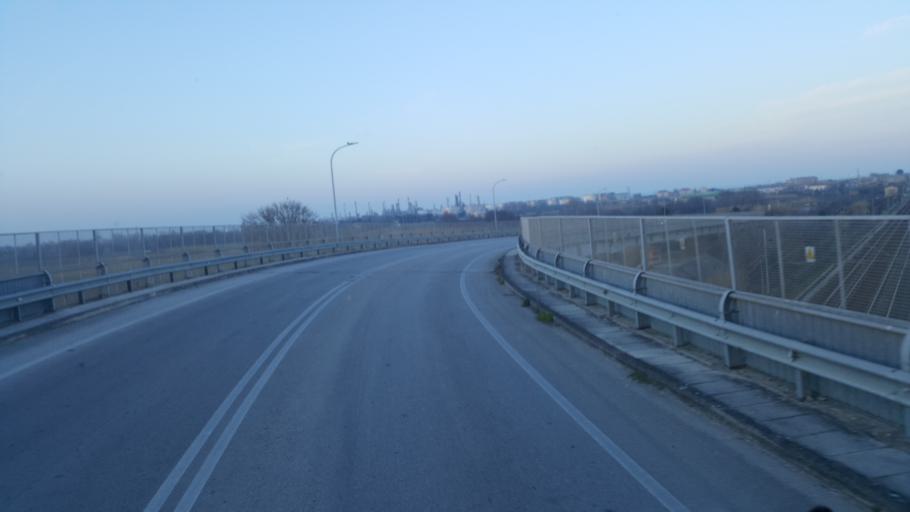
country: IT
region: The Marches
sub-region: Provincia di Ancona
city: Falconara Marittima
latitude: 43.6230
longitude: 13.3776
